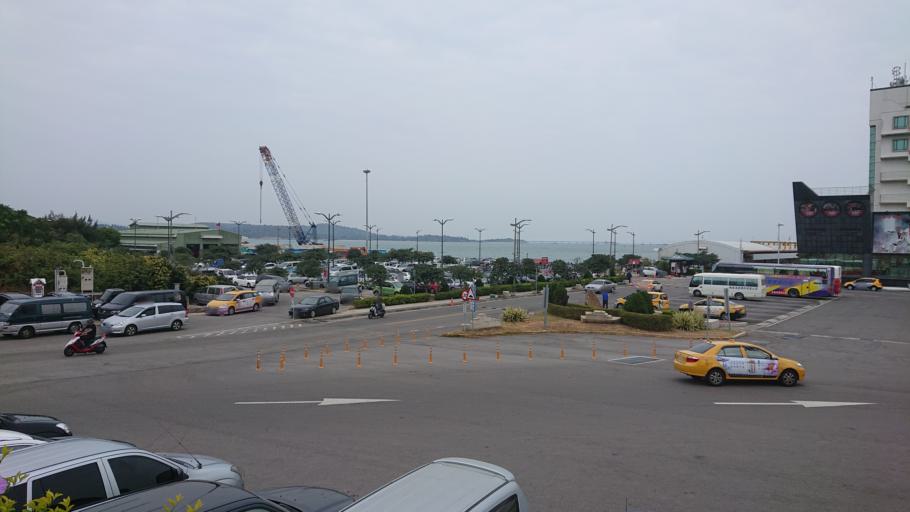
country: TW
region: Fukien
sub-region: Kinmen
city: Jincheng
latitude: 24.4143
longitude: 118.2868
